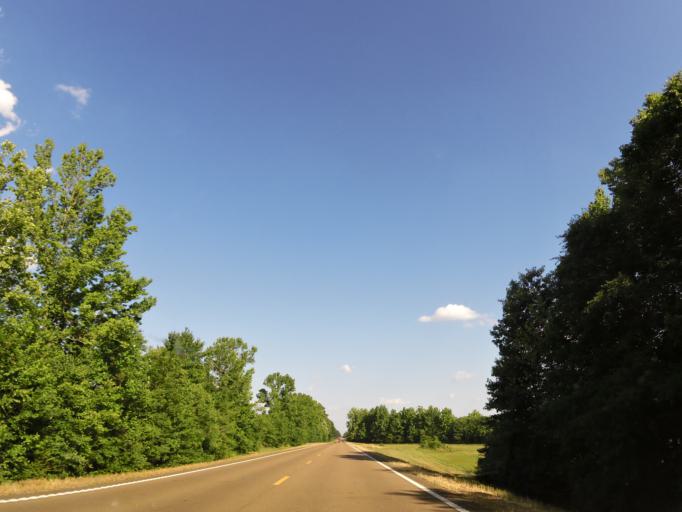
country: US
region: Mississippi
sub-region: Yalobusha County
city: Water Valley
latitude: 34.1690
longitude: -89.4469
